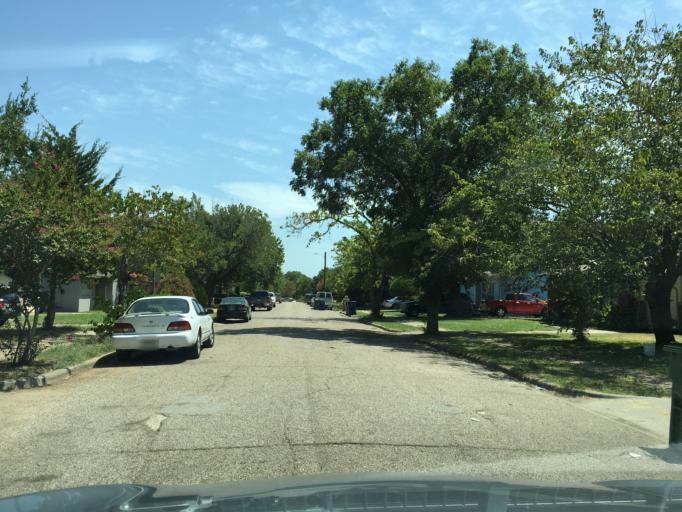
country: US
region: Texas
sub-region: Dallas County
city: Garland
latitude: 32.8951
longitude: -96.6281
